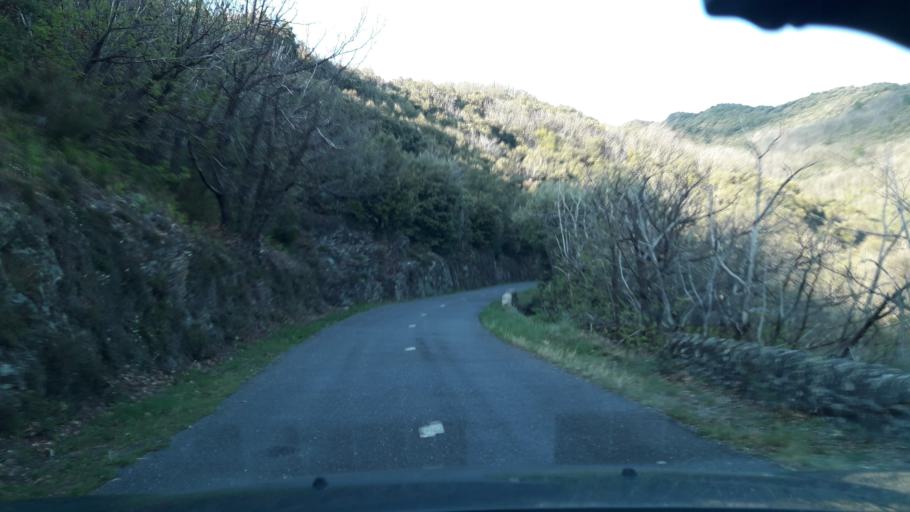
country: FR
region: Languedoc-Roussillon
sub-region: Departement du Gard
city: Valleraugue
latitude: 44.1000
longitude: 3.6376
